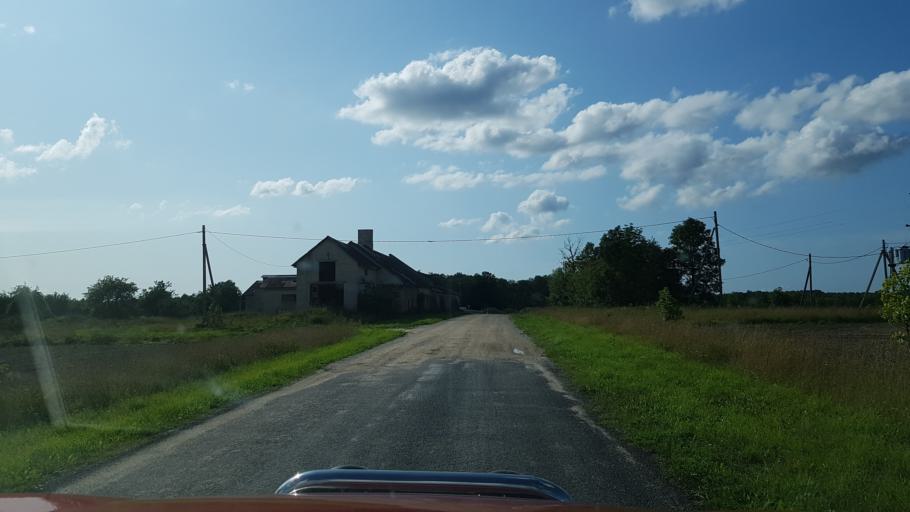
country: EE
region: Harju
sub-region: Paldiski linn
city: Paldiski
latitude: 59.1994
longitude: 23.9448
